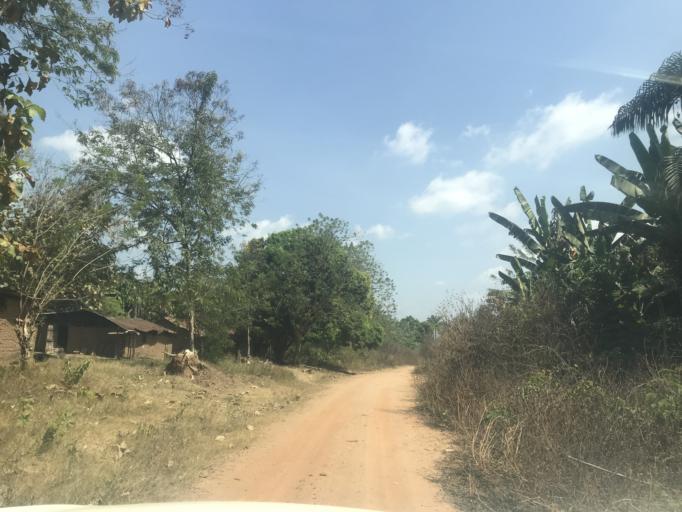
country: NG
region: Osun
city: Otan Ayegbaju
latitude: 7.8955
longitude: 4.8598
